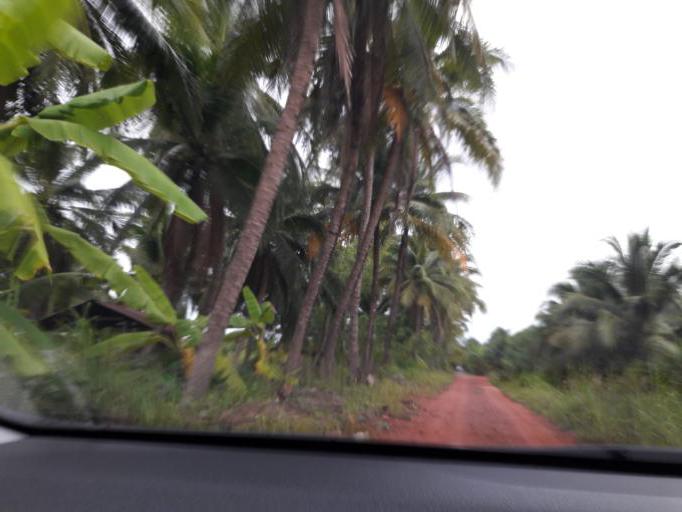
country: TH
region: Samut Sakhon
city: Ban Phaeo
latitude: 13.5465
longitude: 100.0383
